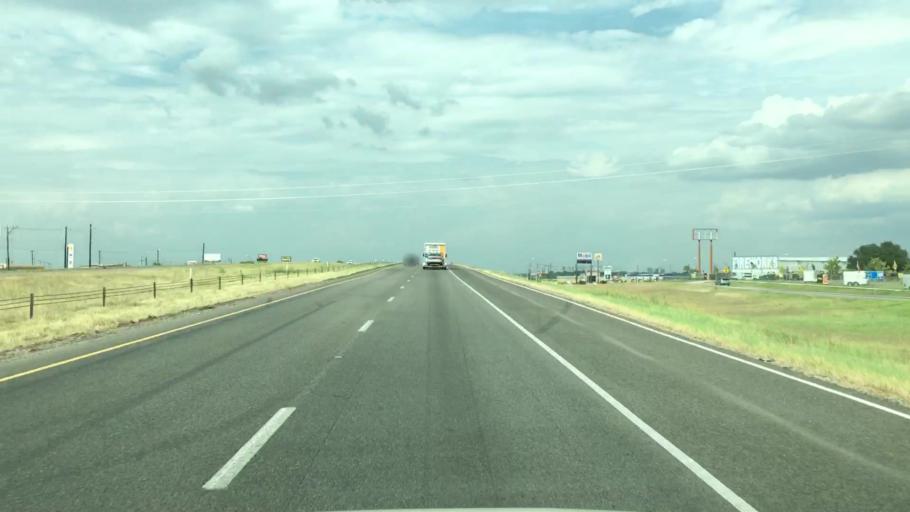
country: US
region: Texas
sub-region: Bexar County
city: Elmendorf
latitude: 29.2152
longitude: -98.4135
